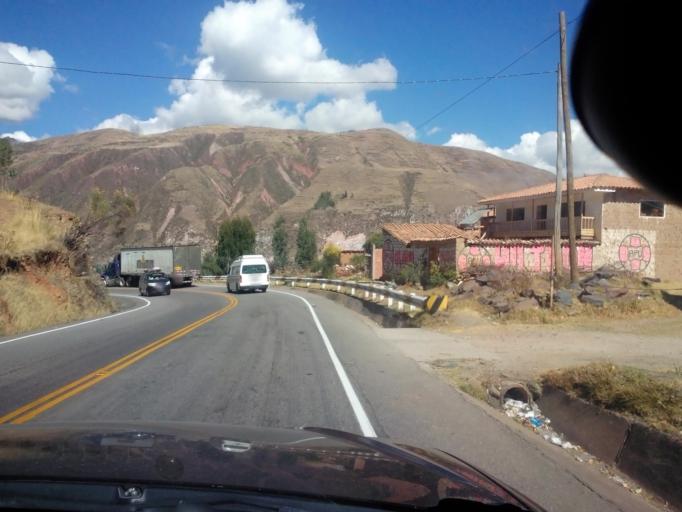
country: PE
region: Cusco
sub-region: Provincia de Quispicanchis
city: Urcos
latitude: -13.6940
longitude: -71.5982
